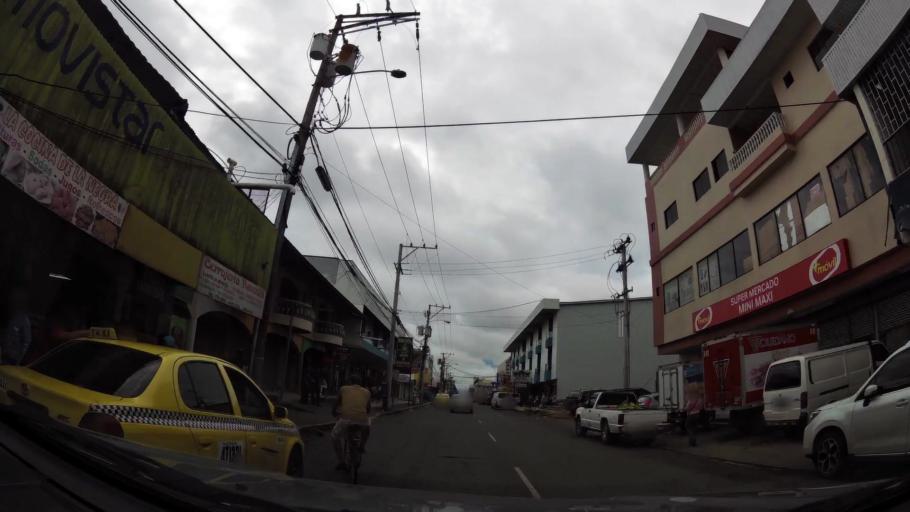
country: PA
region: Chiriqui
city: David
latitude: 8.4311
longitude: -82.4237
